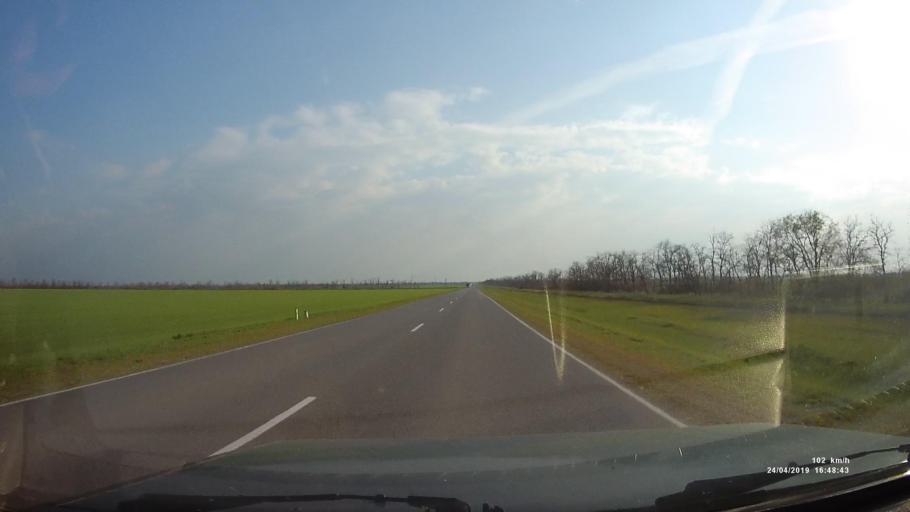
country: RU
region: Rostov
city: Proletarsk
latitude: 46.7271
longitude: 41.7722
